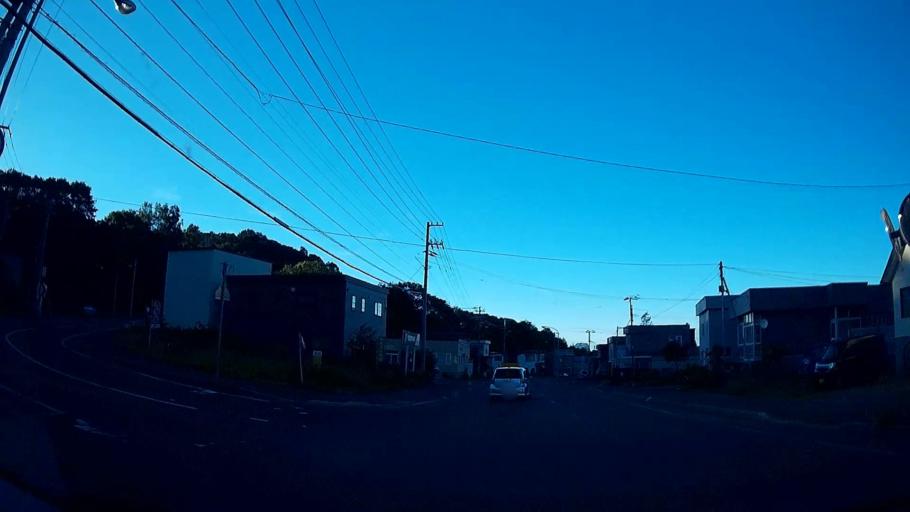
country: JP
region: Hokkaido
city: Otaru
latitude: 43.1554
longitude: 141.0416
